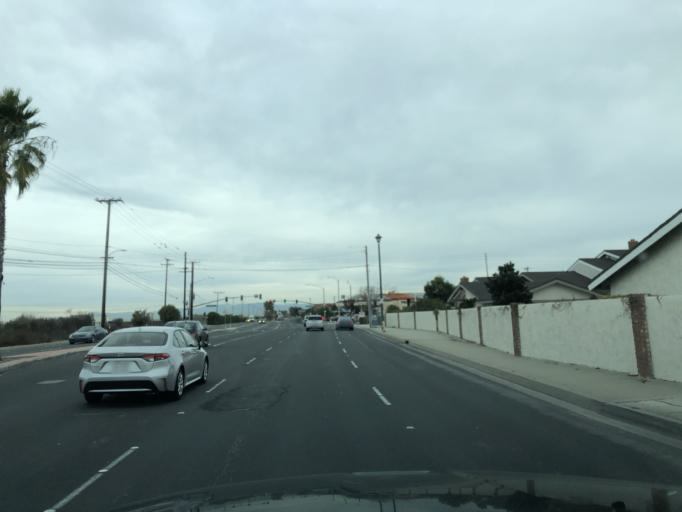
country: US
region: California
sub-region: Orange County
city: Westminster
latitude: 33.7579
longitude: -118.0425
